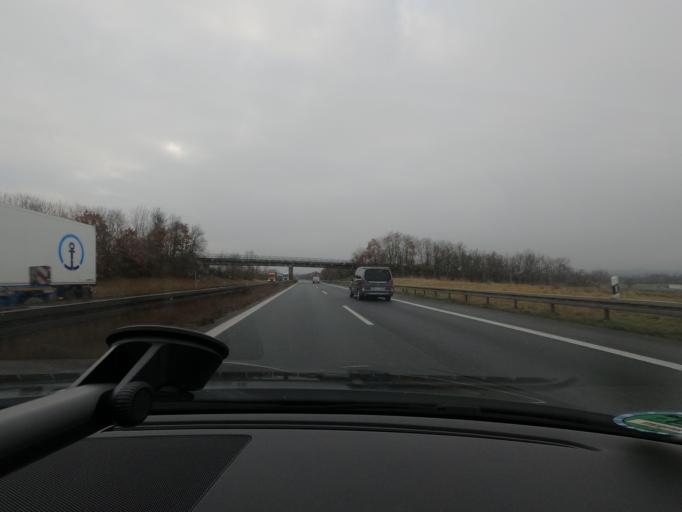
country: DE
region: Bavaria
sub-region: Upper Franconia
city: Altendorf
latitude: 49.8182
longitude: 11.0104
